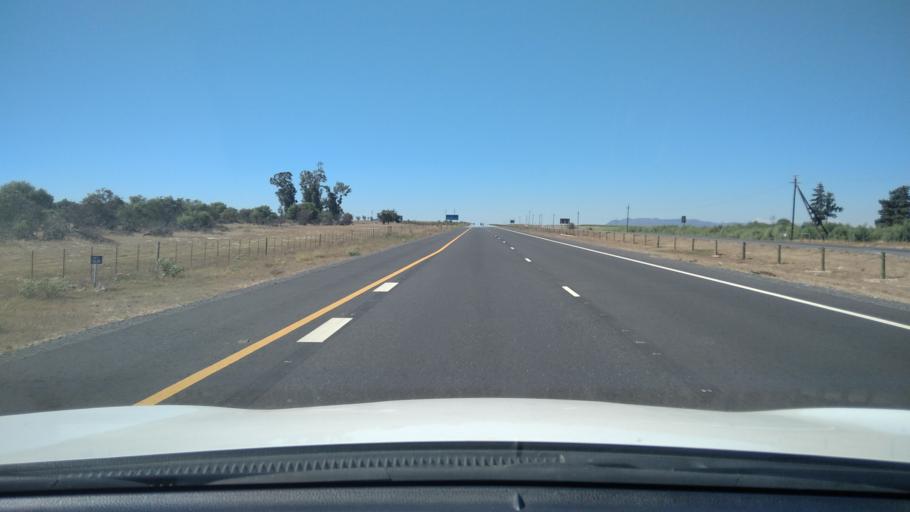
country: ZA
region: Western Cape
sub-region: West Coast District Municipality
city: Malmesbury
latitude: -33.5601
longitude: 18.6262
